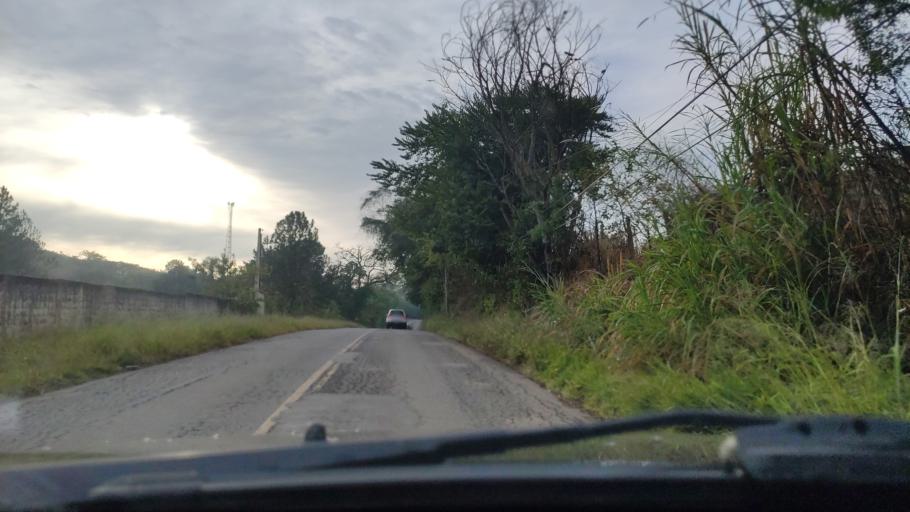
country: BR
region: Sao Paulo
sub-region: Jarinu
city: Jarinu
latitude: -23.1202
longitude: -46.7663
